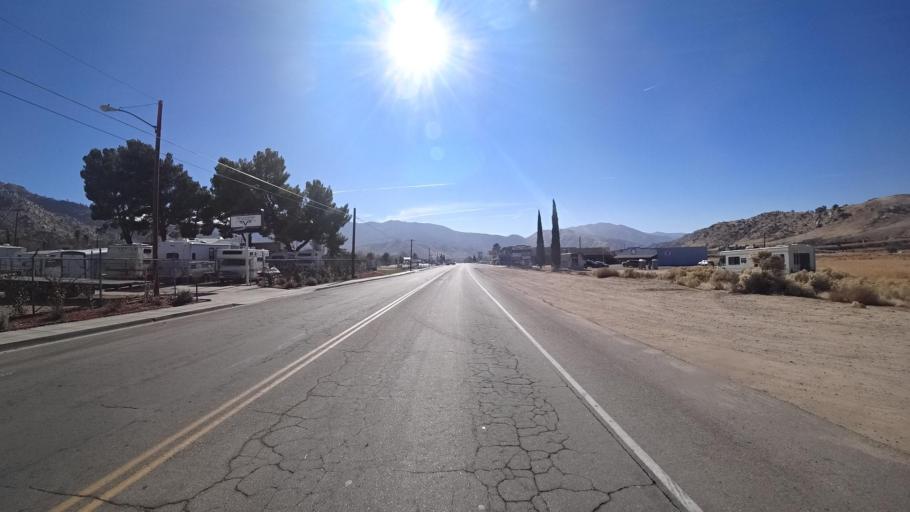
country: US
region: California
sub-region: Kern County
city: Lake Isabella
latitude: 35.6310
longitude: -118.4729
